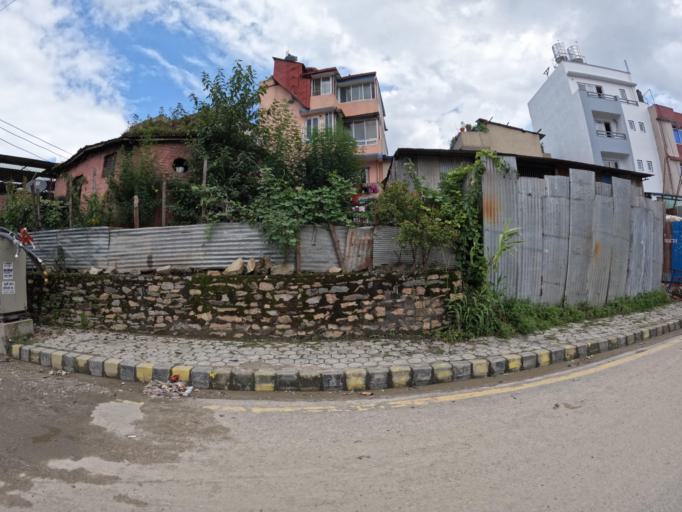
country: NP
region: Central Region
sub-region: Bagmati Zone
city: Kathmandu
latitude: 27.7468
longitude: 85.3151
